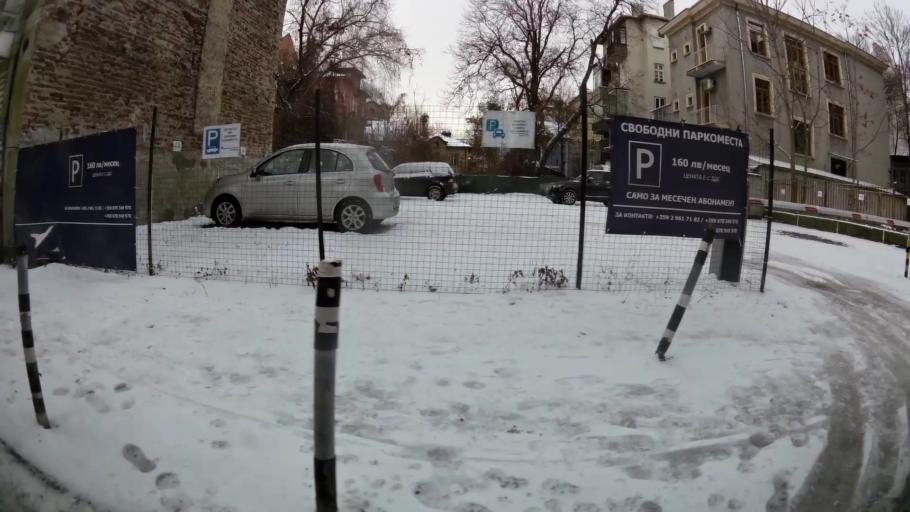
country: BG
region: Sofia-Capital
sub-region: Stolichna Obshtina
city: Sofia
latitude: 42.7008
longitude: 23.3276
